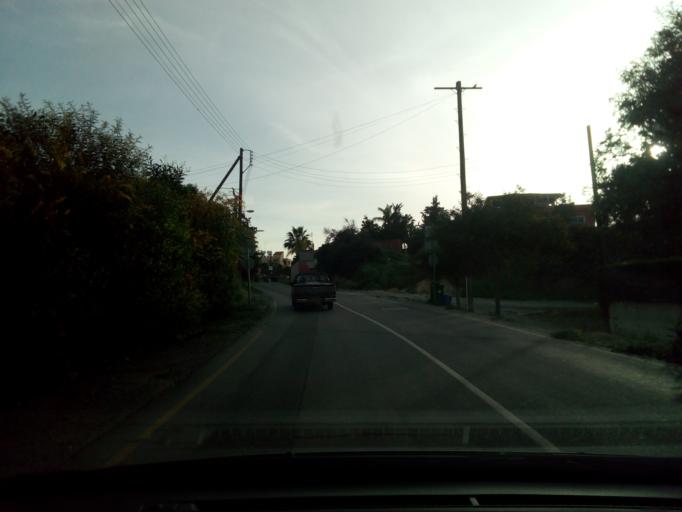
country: CY
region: Larnaka
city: Agios Tychon
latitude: 34.7172
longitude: 33.1303
